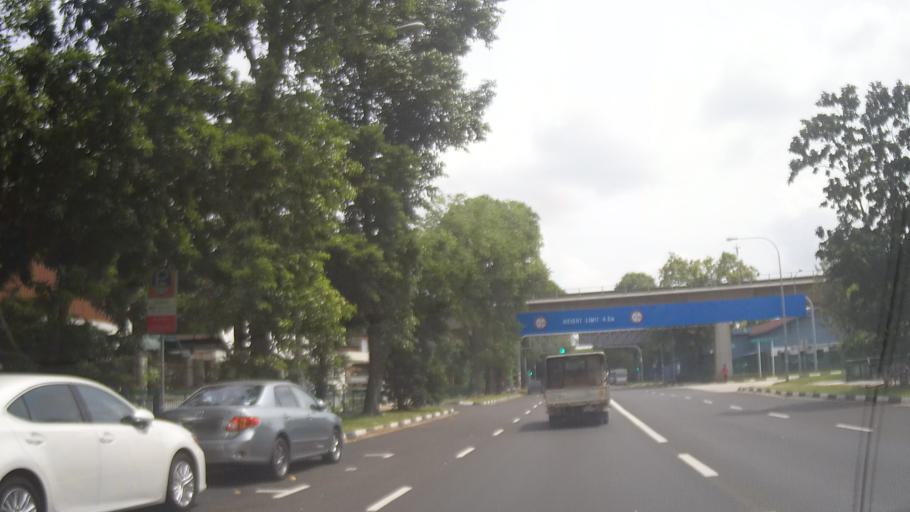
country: MY
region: Johor
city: Johor Bahru
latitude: 1.4167
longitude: 103.7474
